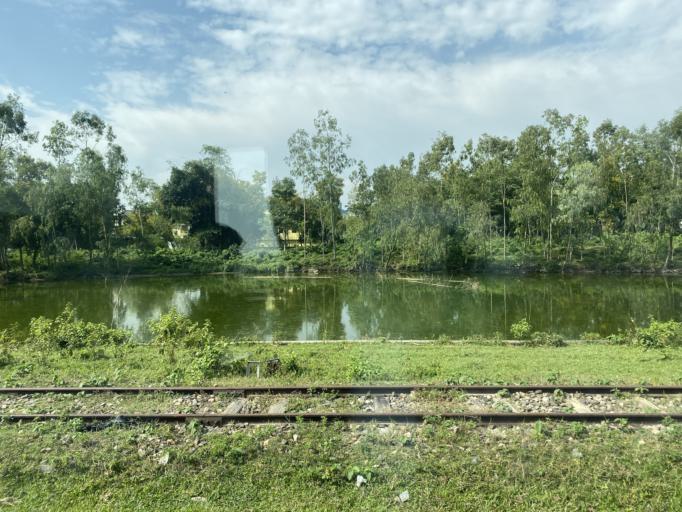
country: BD
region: Sylhet
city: Habiganj
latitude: 24.1770
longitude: 91.3575
